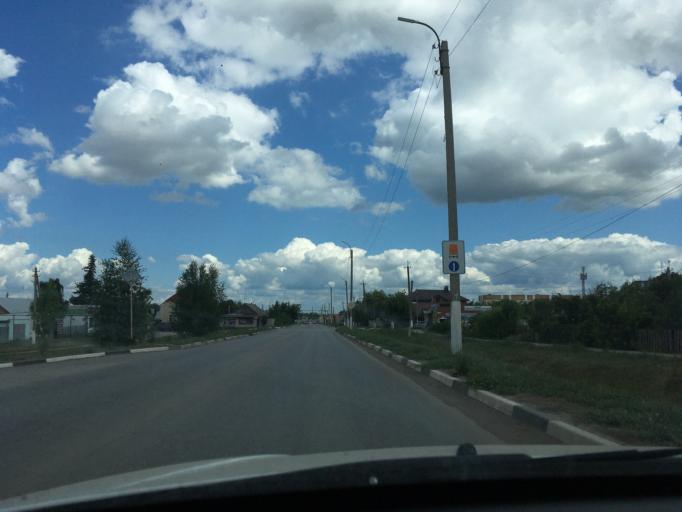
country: RU
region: Samara
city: Bezenchuk
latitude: 52.9882
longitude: 49.4351
